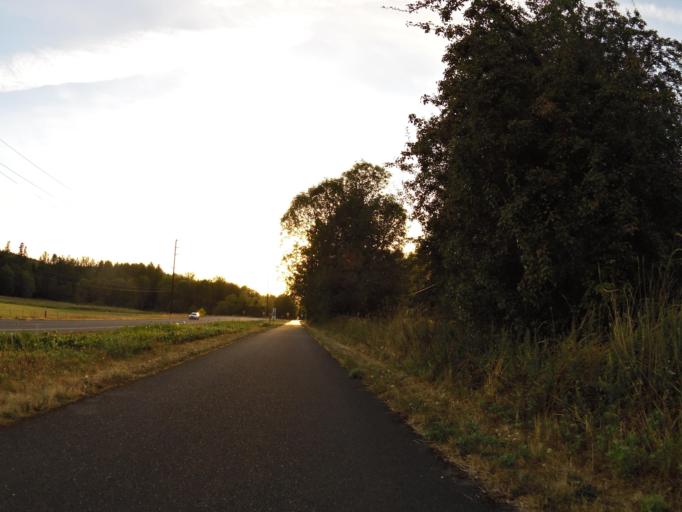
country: US
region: Washington
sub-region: Thurston County
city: Tenino
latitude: 46.8587
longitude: -122.7988
